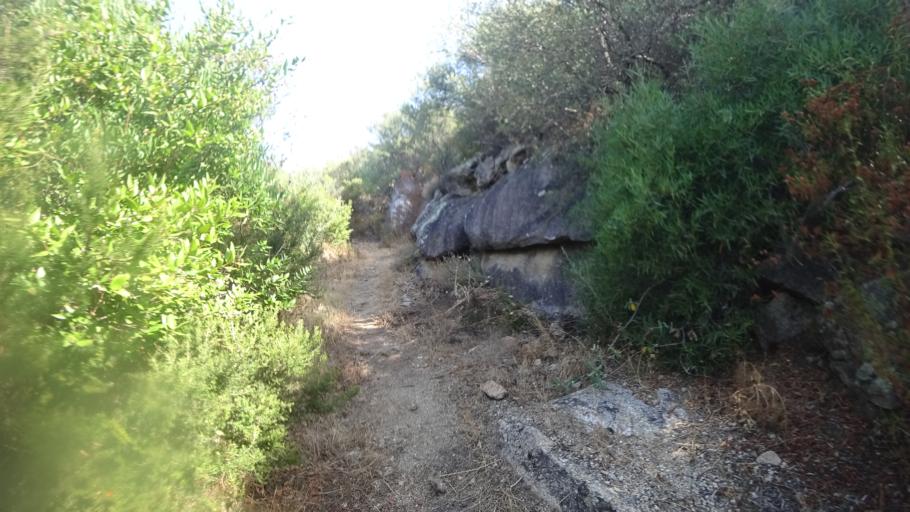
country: FR
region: Corsica
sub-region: Departement de la Corse-du-Sud
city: Porto-Vecchio
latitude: 41.6645
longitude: 9.3265
